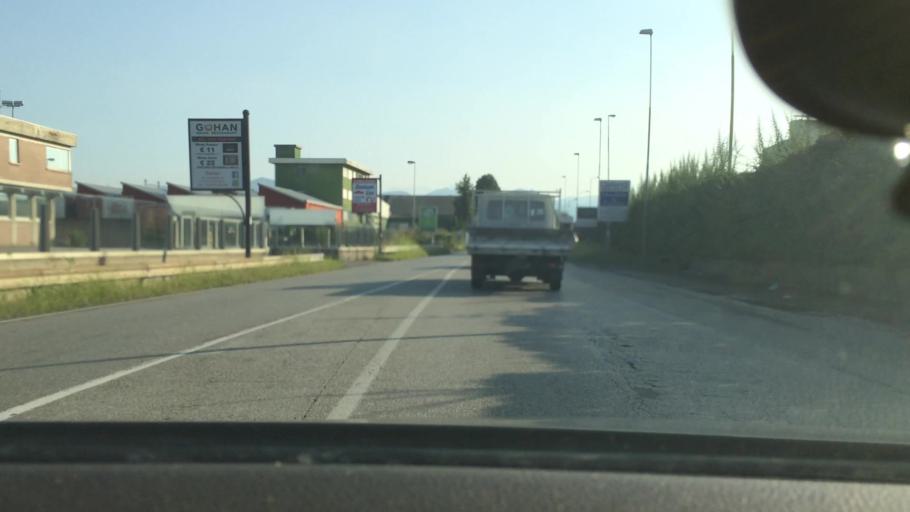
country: IT
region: Lombardy
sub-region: Provincia di Bergamo
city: Lallio
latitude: 45.6565
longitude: 9.6260
